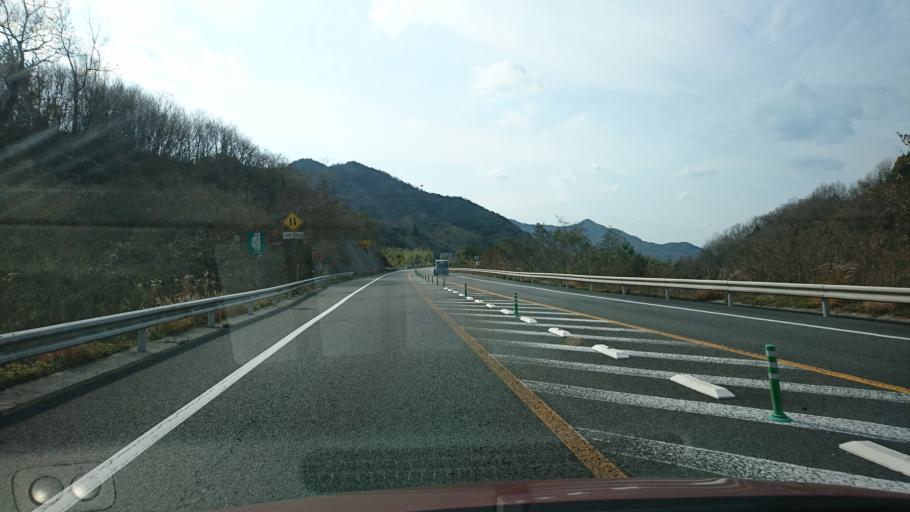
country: JP
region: Hiroshima
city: Innoshima
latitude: 34.1371
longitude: 133.0533
